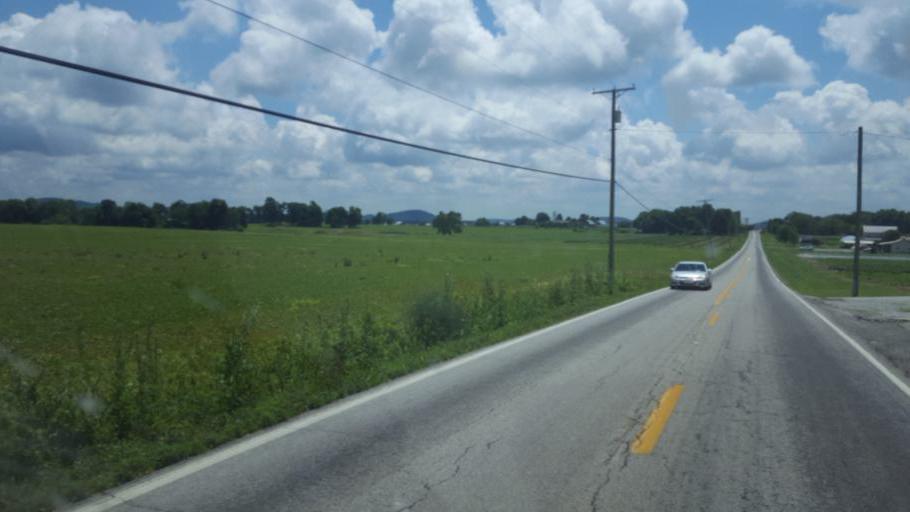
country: US
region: Ohio
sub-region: Highland County
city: Greenfield
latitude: 39.2262
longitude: -83.4247
